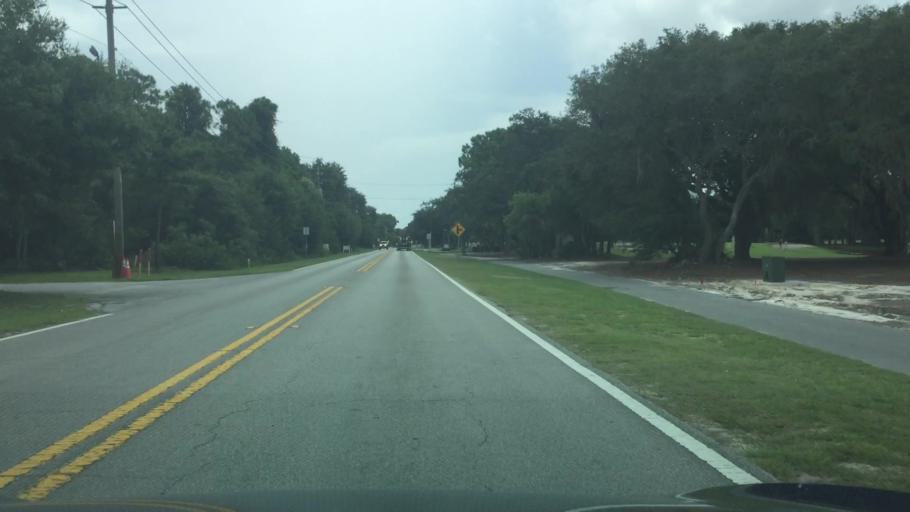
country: US
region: Florida
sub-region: Bay County
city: Upper Grand Lagoon
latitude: 30.1549
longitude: -85.7293
